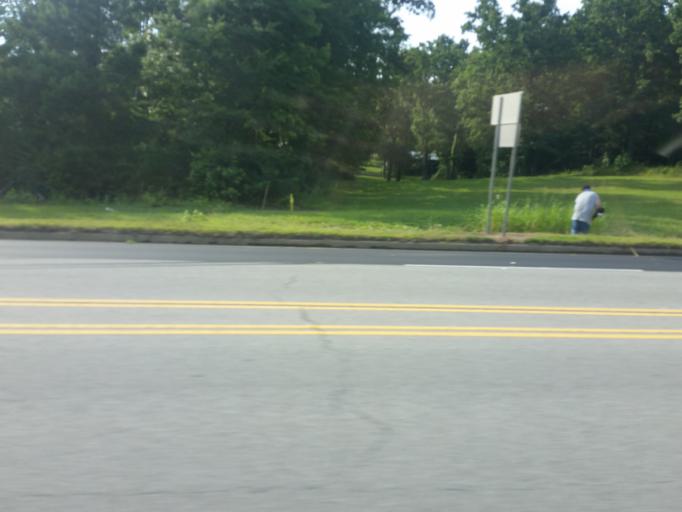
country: US
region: Tennessee
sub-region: Humphreys County
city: Johnsonville
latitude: 36.0382
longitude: -87.9335
